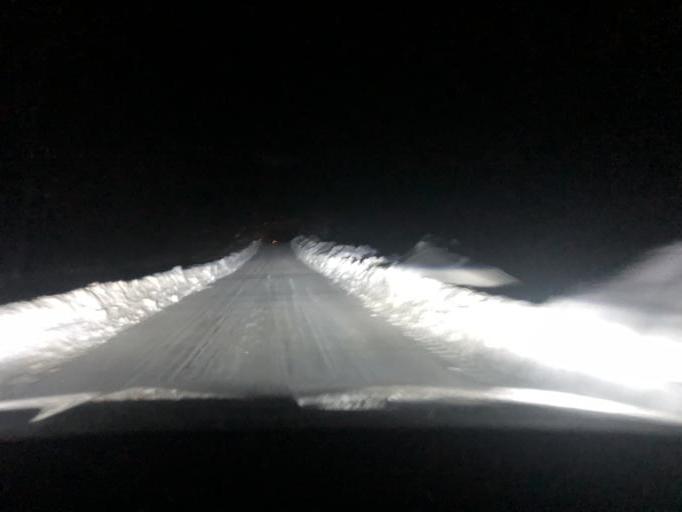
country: SE
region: Vaesterbotten
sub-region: Skelleftea Kommun
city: Byske
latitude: 65.0300
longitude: 21.3310
